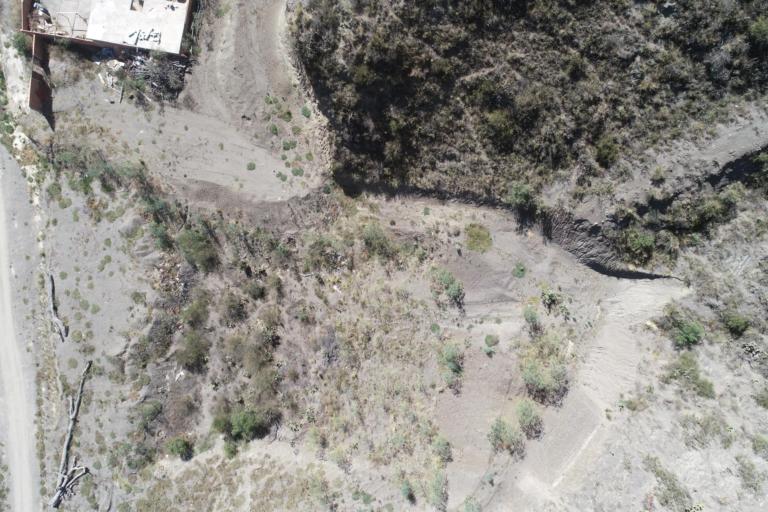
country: BO
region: La Paz
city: La Paz
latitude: -16.6330
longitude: -68.0458
